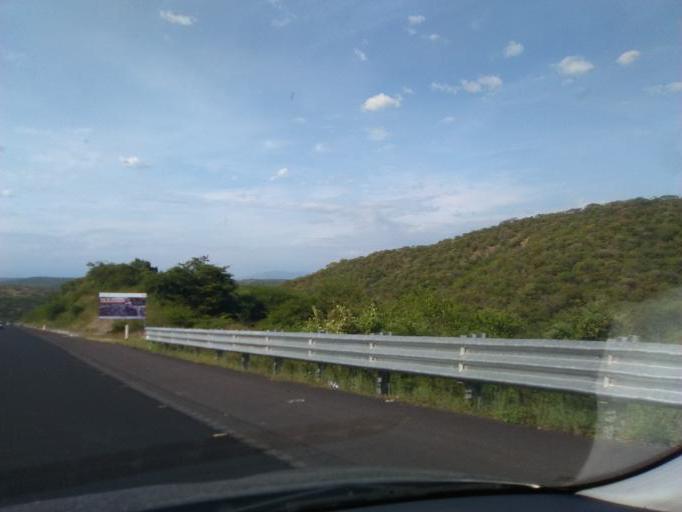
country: MX
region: Morelos
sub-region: Jojutla
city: Higueron
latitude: 18.5048
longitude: -99.1927
